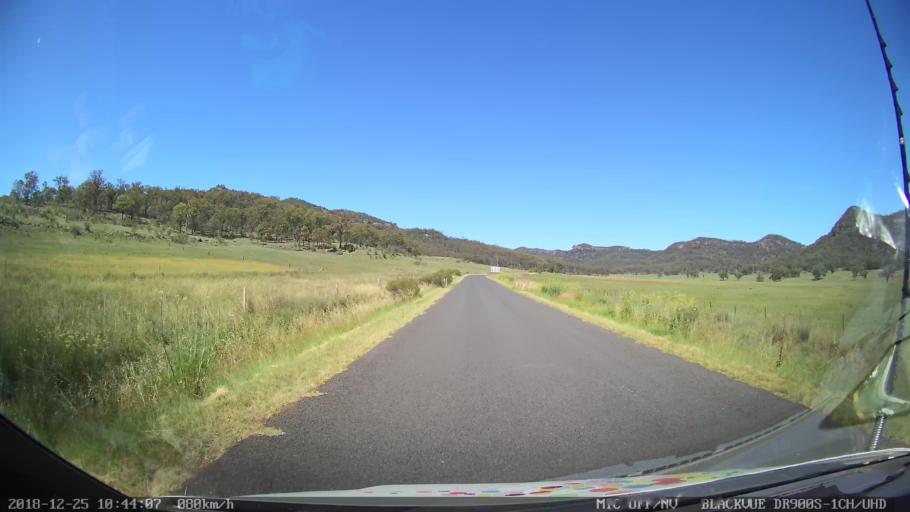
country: AU
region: New South Wales
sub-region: Upper Hunter Shire
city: Merriwa
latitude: -32.4266
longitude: 150.3045
